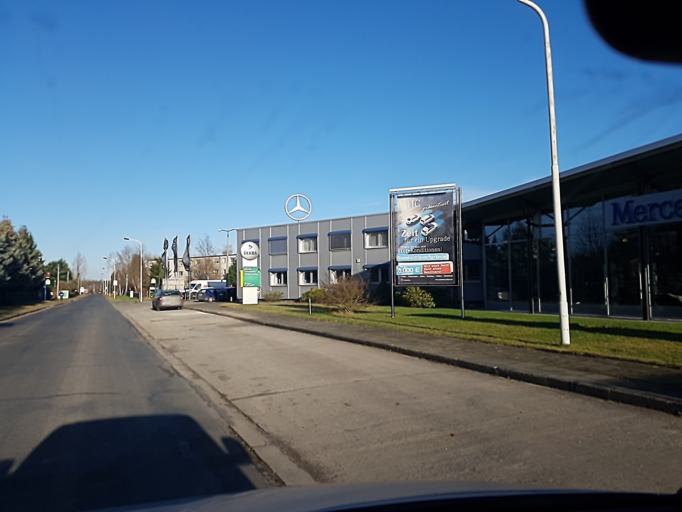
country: DE
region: Brandenburg
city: Finsterwalde
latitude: 51.6422
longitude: 13.7091
